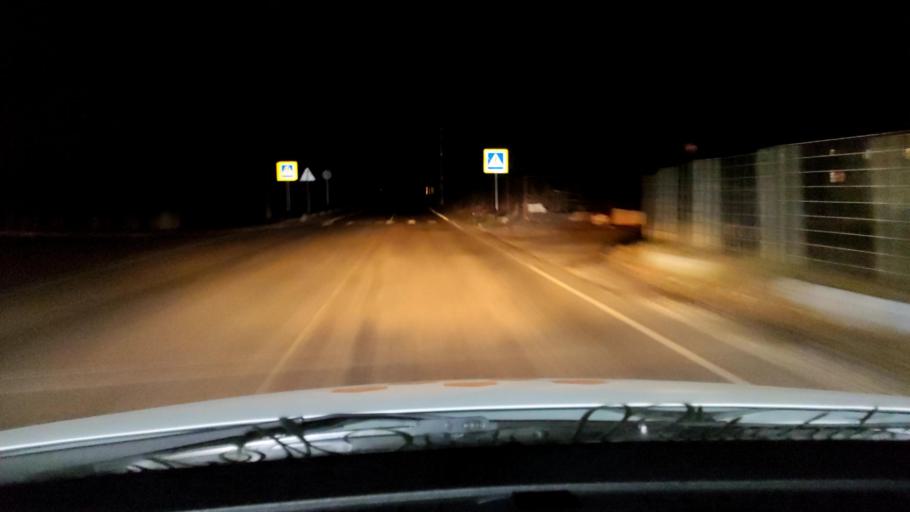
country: RU
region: Voronezj
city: Shilovo
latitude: 51.5368
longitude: 39.1390
